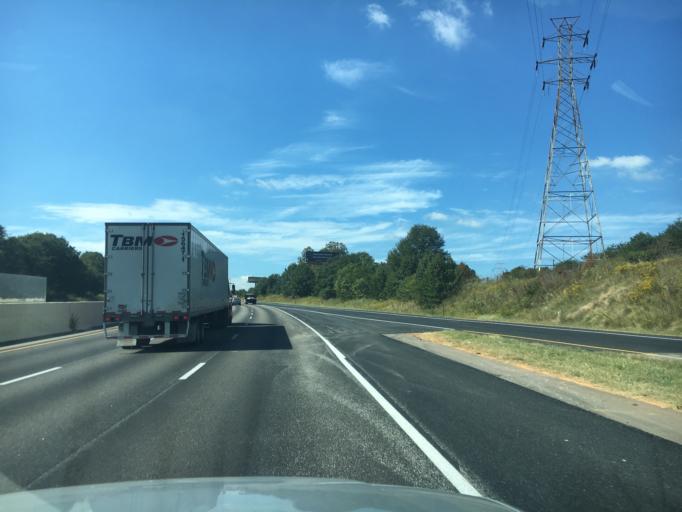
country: US
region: South Carolina
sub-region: Spartanburg County
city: Fairforest
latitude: 34.9599
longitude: -82.0565
